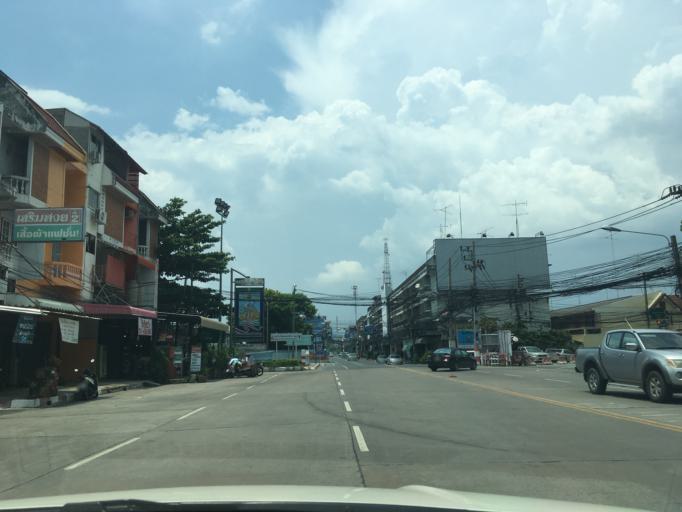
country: TH
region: Chon Buri
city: Chon Buri
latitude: 13.3569
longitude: 100.9783
